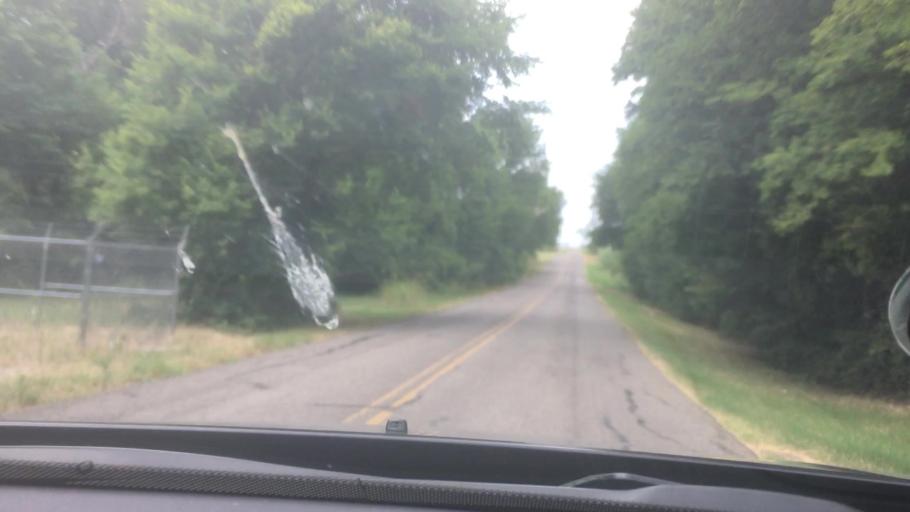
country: US
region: Oklahoma
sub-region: Murray County
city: Davis
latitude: 34.4956
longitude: -97.0554
